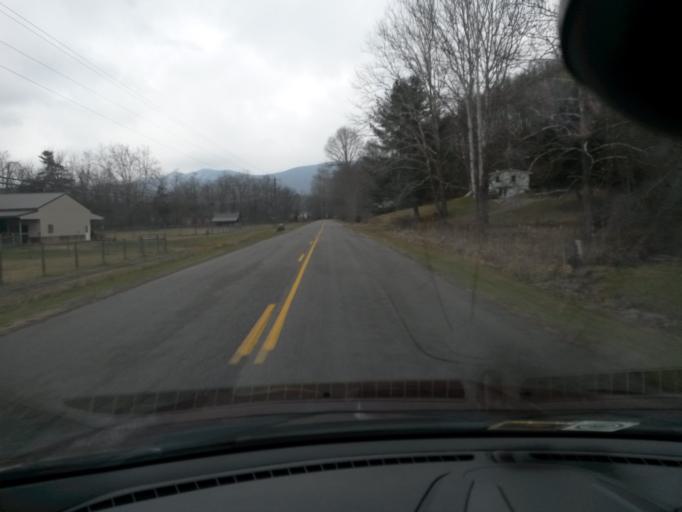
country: US
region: Virginia
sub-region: City of Lexington
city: Lexington
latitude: 37.8658
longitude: -79.5342
